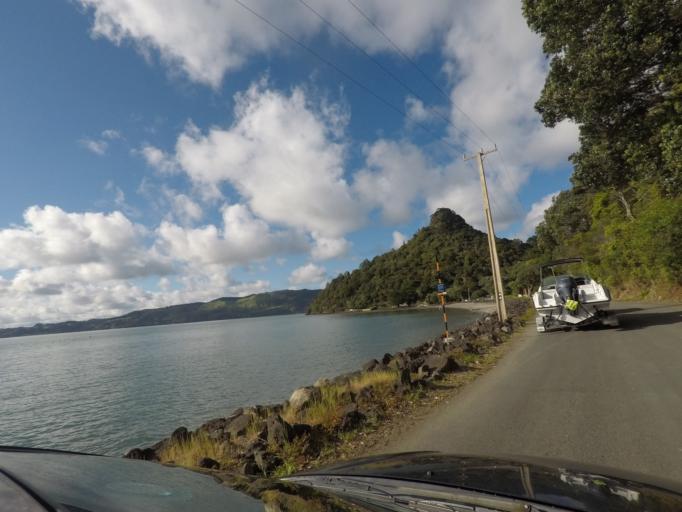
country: NZ
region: Auckland
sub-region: Auckland
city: Titirangi
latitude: -37.0140
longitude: 174.5594
